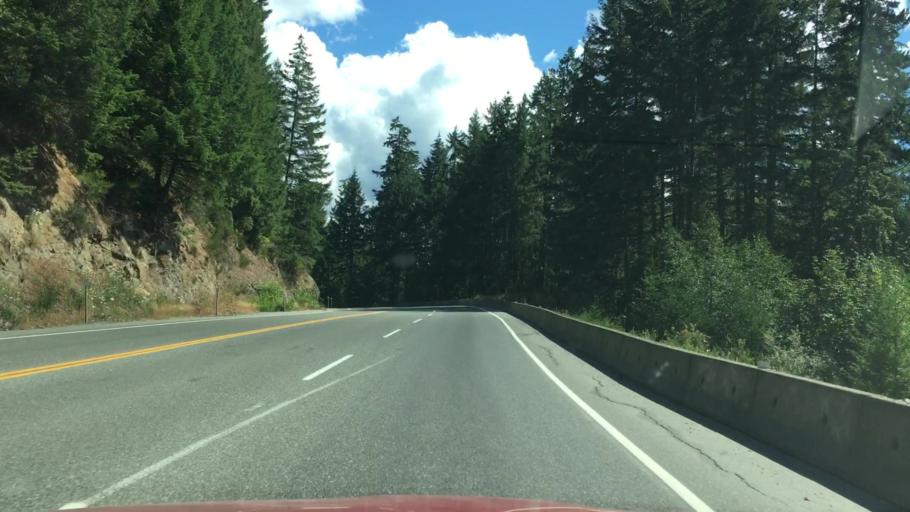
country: CA
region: British Columbia
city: Port Alberni
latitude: 49.2657
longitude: -124.7314
